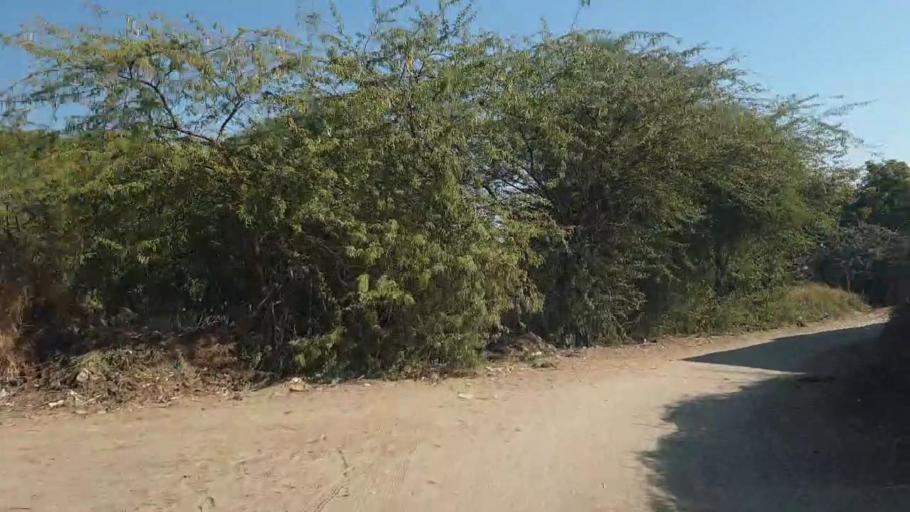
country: PK
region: Sindh
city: Shahpur Chakar
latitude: 26.0830
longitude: 68.5988
